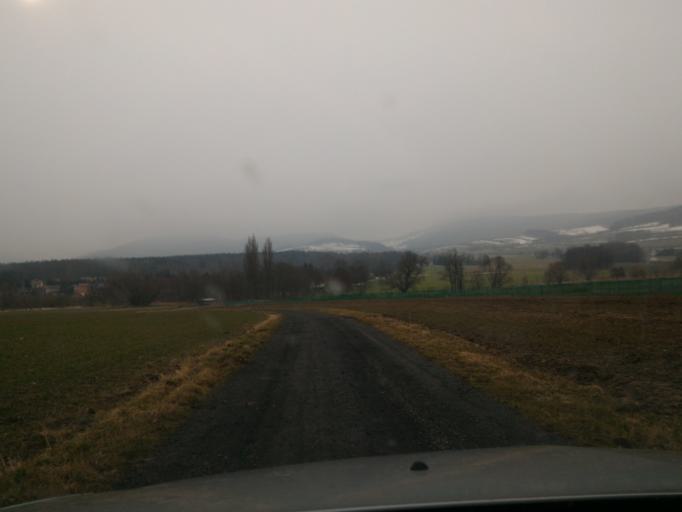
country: CZ
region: Ustecky
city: Varnsdorf
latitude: 50.8885
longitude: 14.6424
